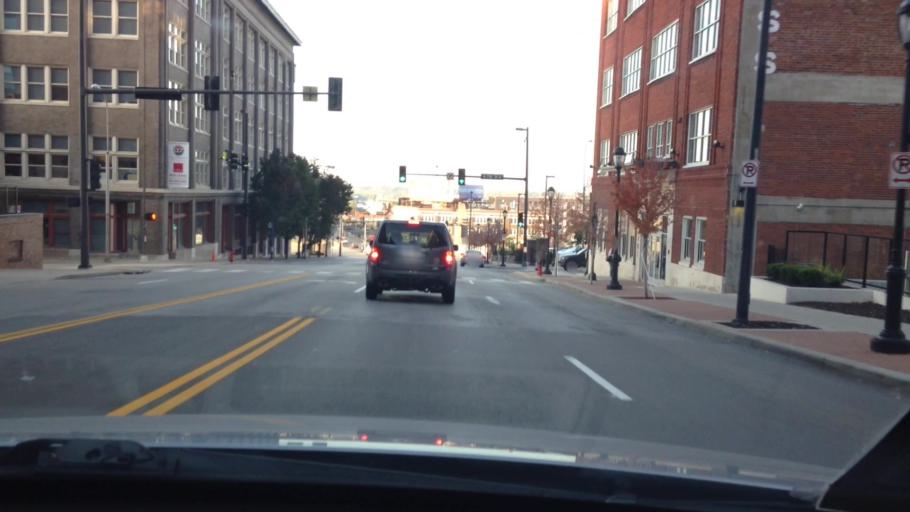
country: US
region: Missouri
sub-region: Jackson County
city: Kansas City
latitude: 39.1051
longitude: -94.5882
